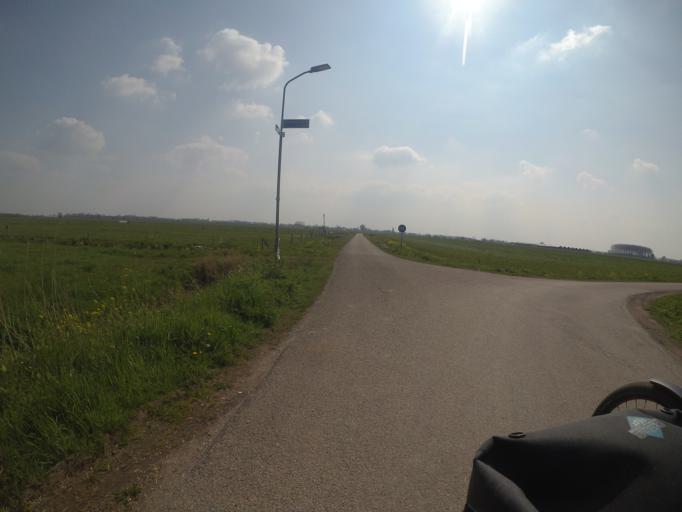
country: NL
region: Gelderland
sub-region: Gemeente Druten
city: Druten
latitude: 51.8652
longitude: 5.5536
